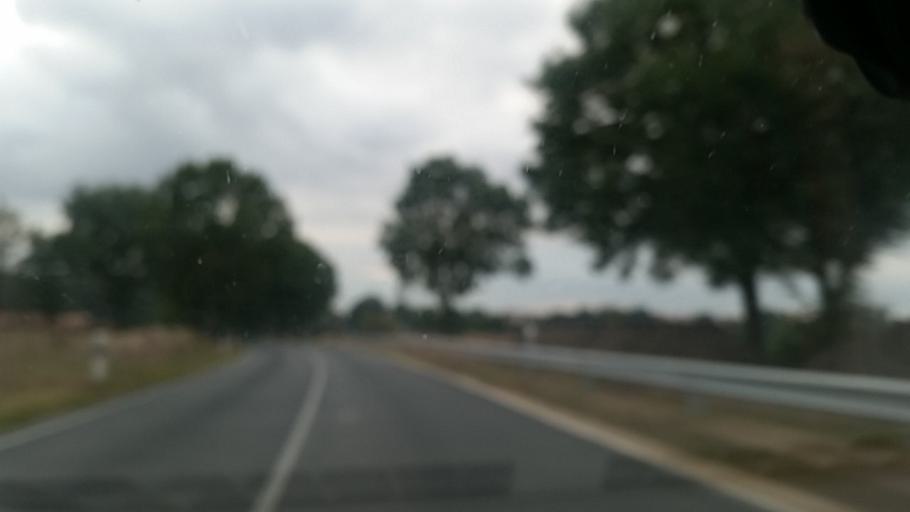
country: DE
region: Lower Saxony
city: Hankensbuttel
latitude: 52.7319
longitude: 10.5890
